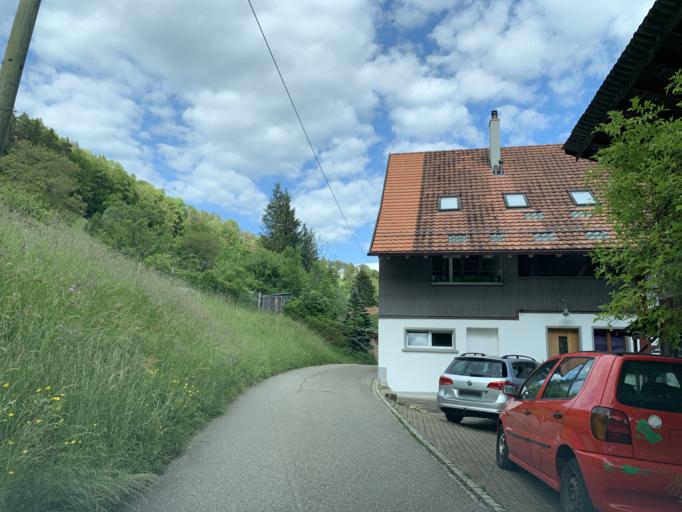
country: CH
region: Zurich
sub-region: Bezirk Winterthur
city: Wuelflingen (Kreis 6) / Niederfeld
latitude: 47.4967
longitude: 8.6796
